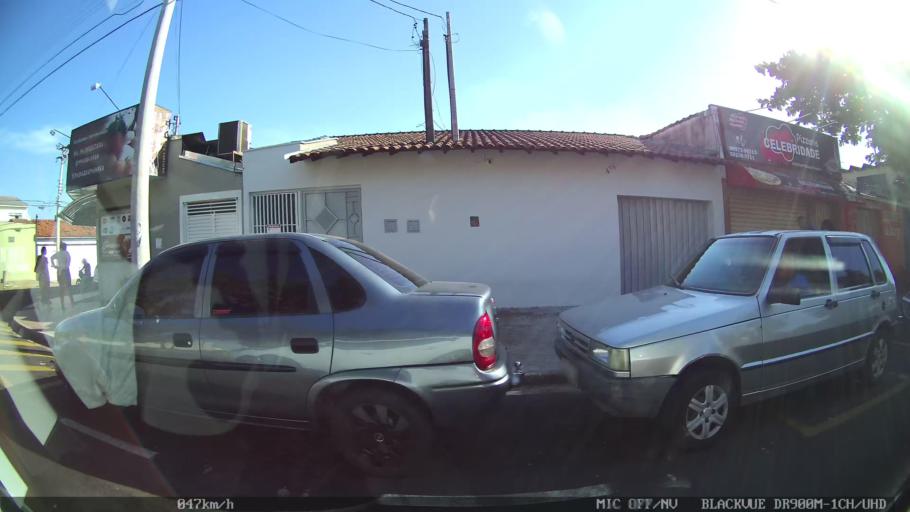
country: BR
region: Sao Paulo
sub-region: Franca
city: Franca
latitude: -20.5073
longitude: -47.4159
